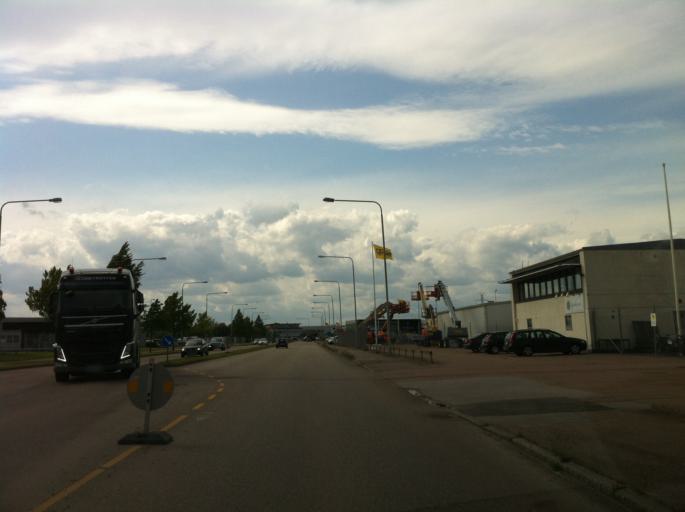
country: SE
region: Skane
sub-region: Landskrona
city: Landskrona
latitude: 55.8670
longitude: 12.8551
